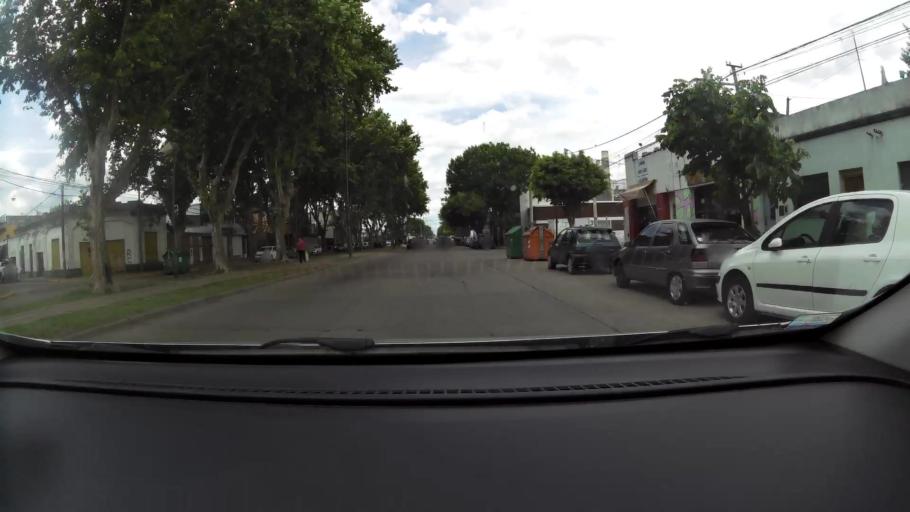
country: AR
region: Santa Fe
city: Gobernador Galvez
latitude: -32.9908
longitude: -60.6481
